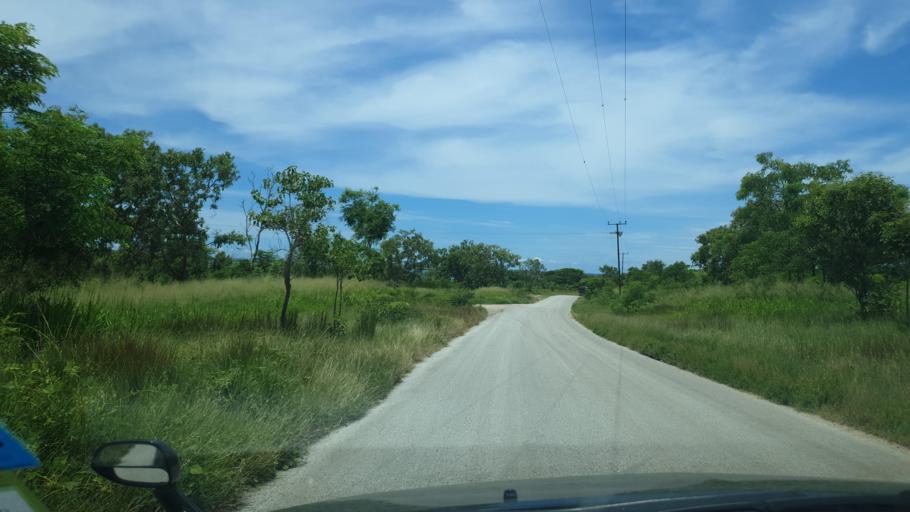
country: PG
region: National Capital
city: Port Moresby
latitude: -9.4299
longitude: 147.0577
